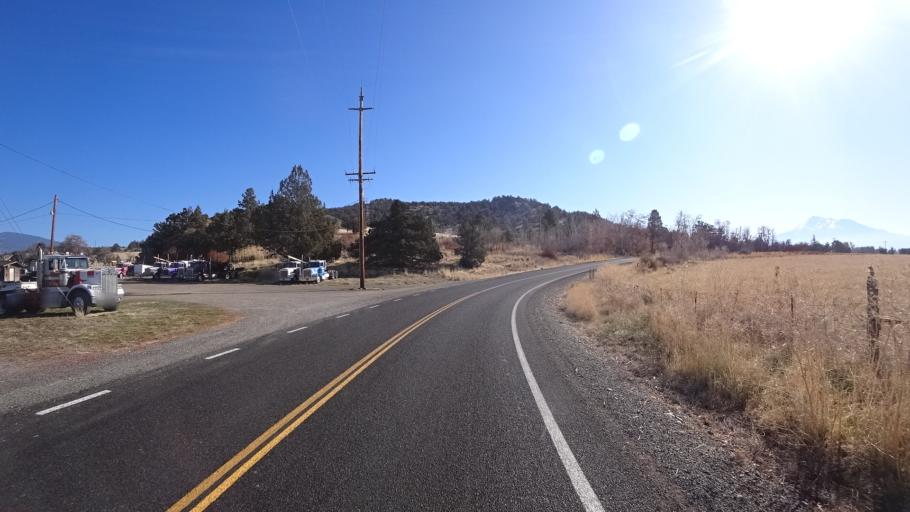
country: US
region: California
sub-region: Siskiyou County
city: Montague
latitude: 41.7113
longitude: -122.3805
